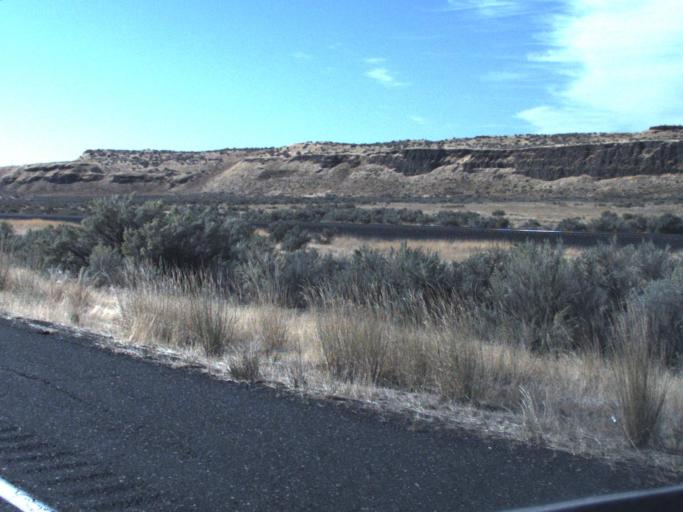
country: US
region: Washington
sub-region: Franklin County
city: Basin City
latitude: 46.4714
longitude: -119.0120
